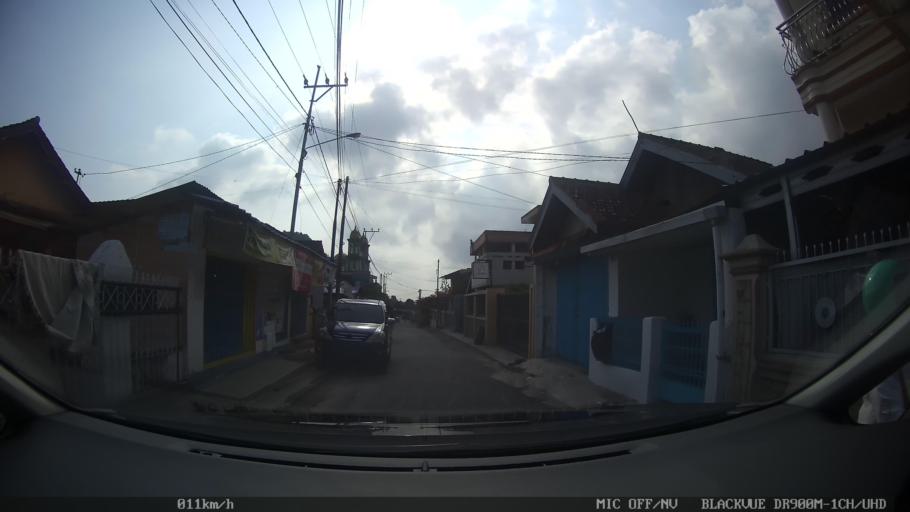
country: ID
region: Lampung
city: Kedaton
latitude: -5.3915
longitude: 105.2637
